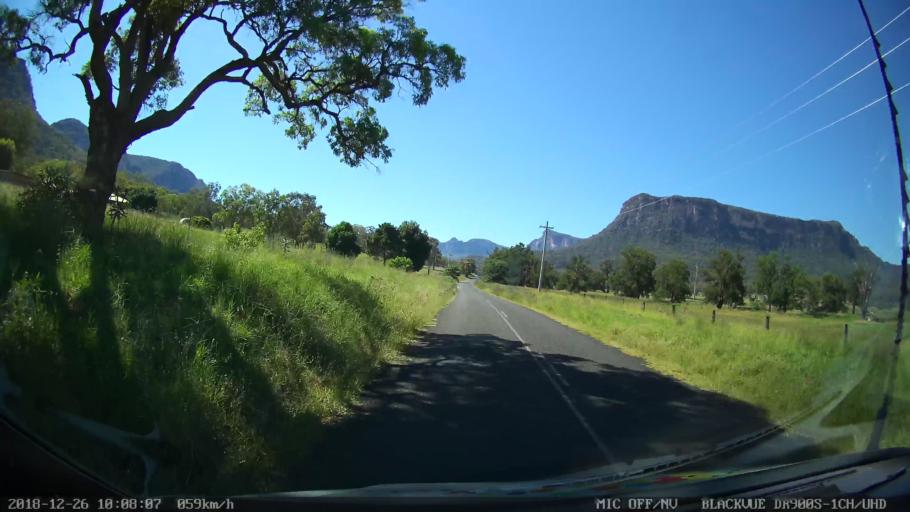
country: AU
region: New South Wales
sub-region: Mid-Western Regional
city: Kandos
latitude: -33.0951
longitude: 150.2285
